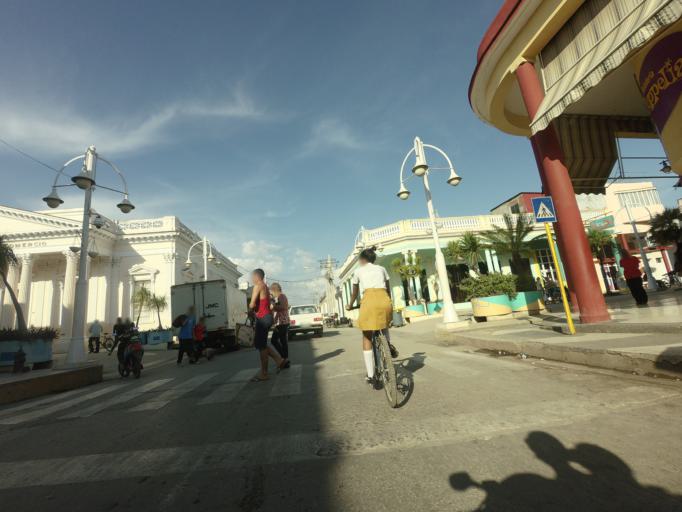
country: CU
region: Ciego de Avila
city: Ciego de Avila
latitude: 21.8425
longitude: -78.7632
